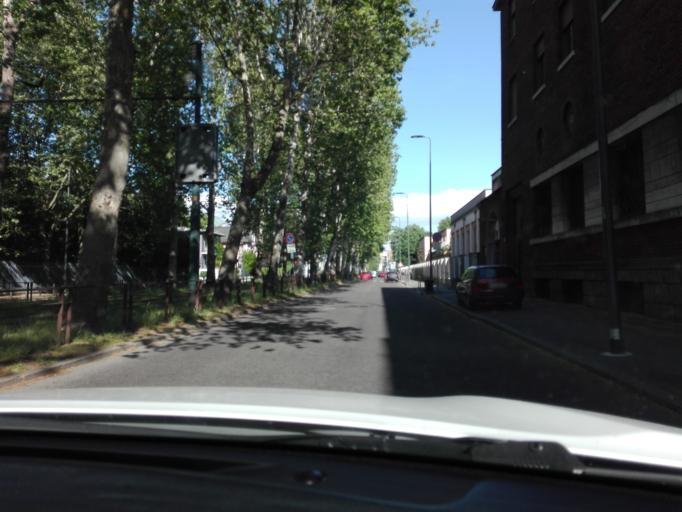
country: IT
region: Lombardy
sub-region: Citta metropolitana di Milano
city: Romano Banco
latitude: 45.4760
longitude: 9.1344
